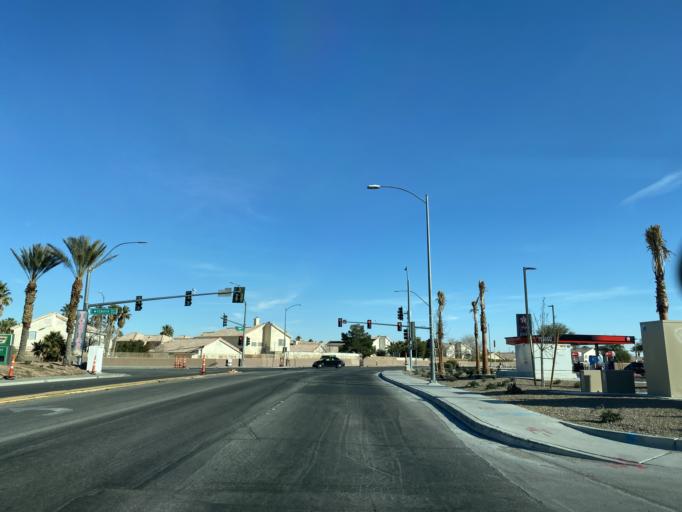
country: US
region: Nevada
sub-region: Clark County
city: Las Vegas
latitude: 36.2647
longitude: -115.2523
